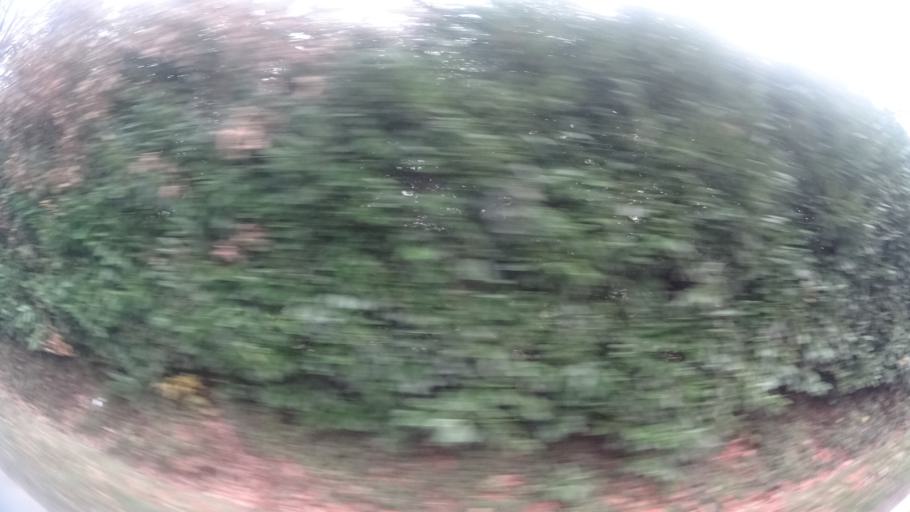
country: FR
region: Brittany
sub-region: Departement d'Ille-et-Vilaine
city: Redon
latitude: 47.6719
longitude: -2.0801
